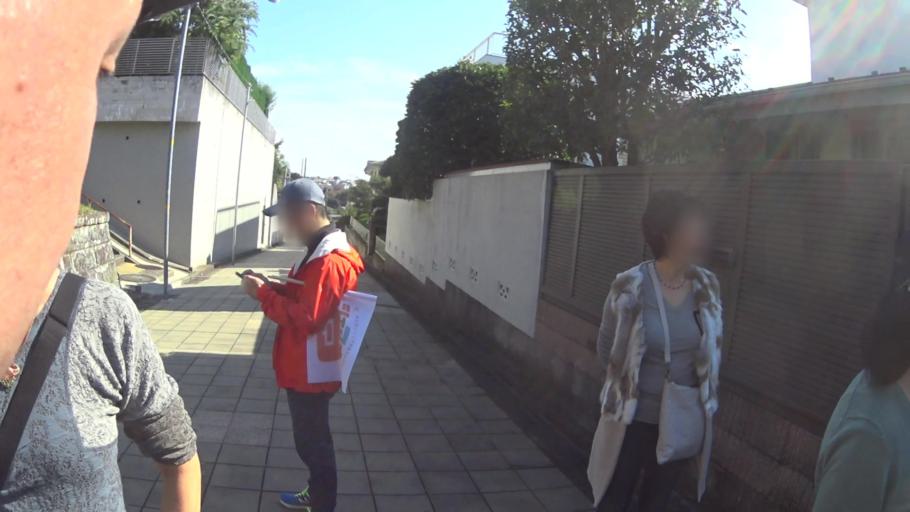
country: JP
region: Tokyo
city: Chofugaoka
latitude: 35.5855
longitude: 139.5511
